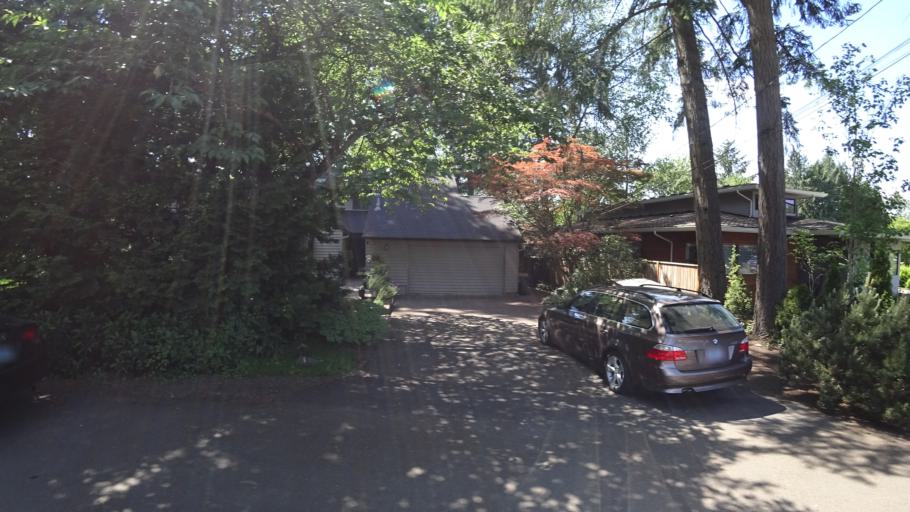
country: US
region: Oregon
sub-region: Clackamas County
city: Lake Oswego
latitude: 45.4293
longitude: -122.7017
